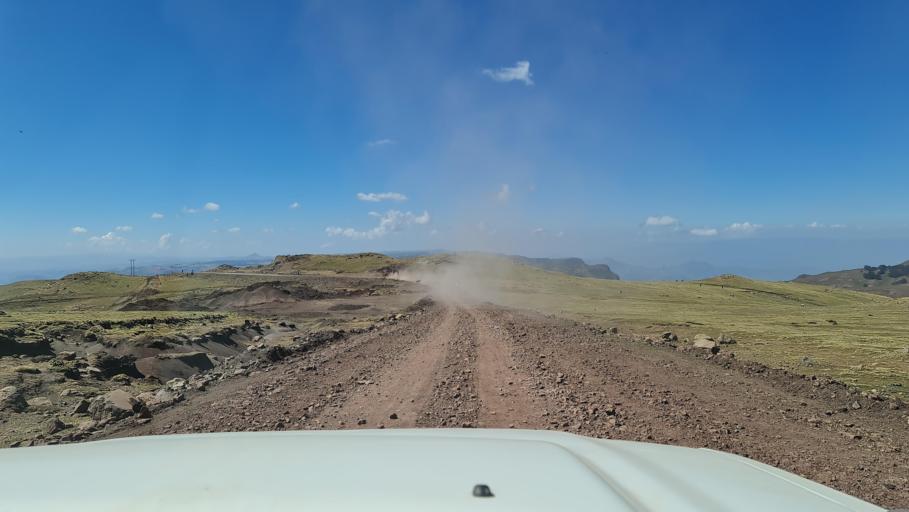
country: ET
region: Amhara
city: Debark'
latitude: 13.2415
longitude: 38.1200
